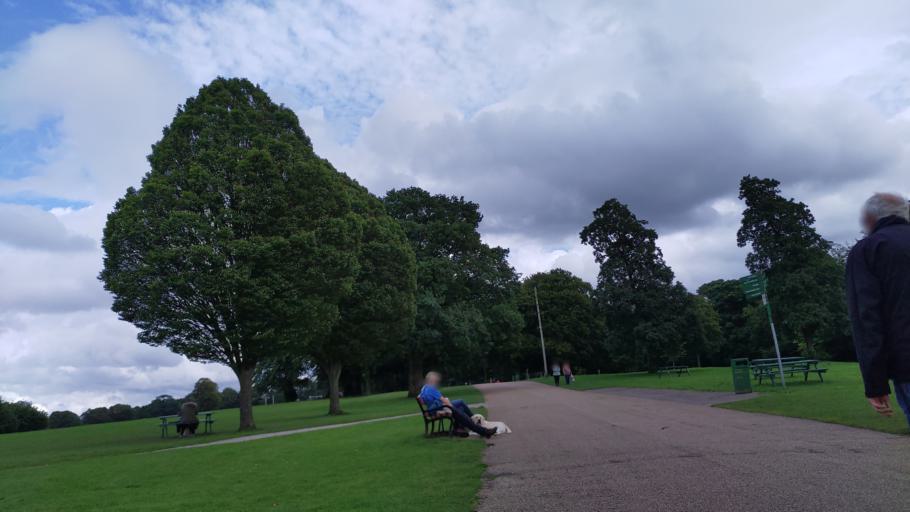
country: GB
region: England
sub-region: Lancashire
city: Chorley
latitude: 53.6580
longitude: -2.6436
